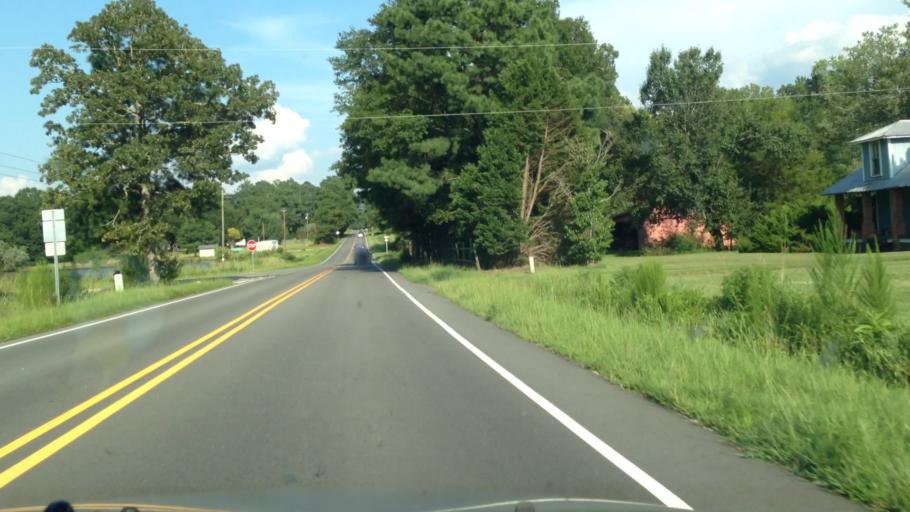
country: US
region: North Carolina
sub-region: Harnett County
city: Buies Creek
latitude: 35.4150
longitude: -78.7093
